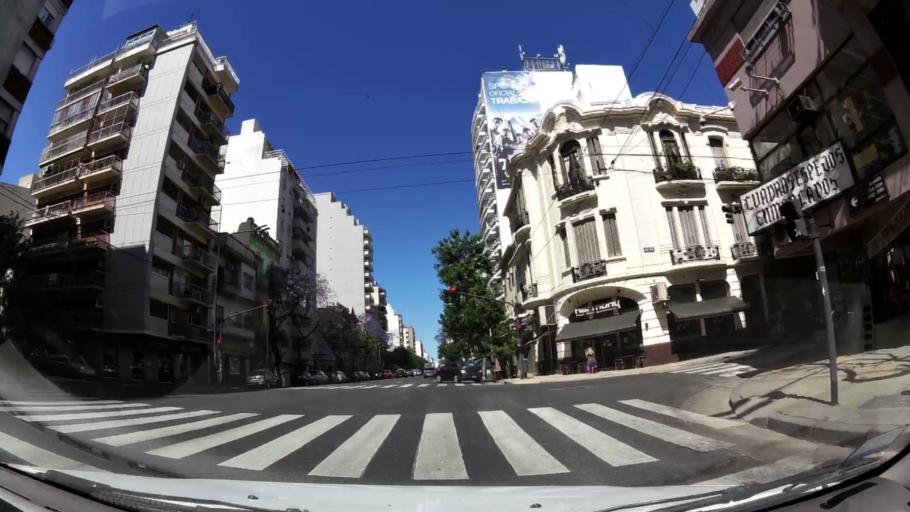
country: AR
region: Buenos Aires F.D.
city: Buenos Aires
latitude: -34.6246
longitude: -58.4090
